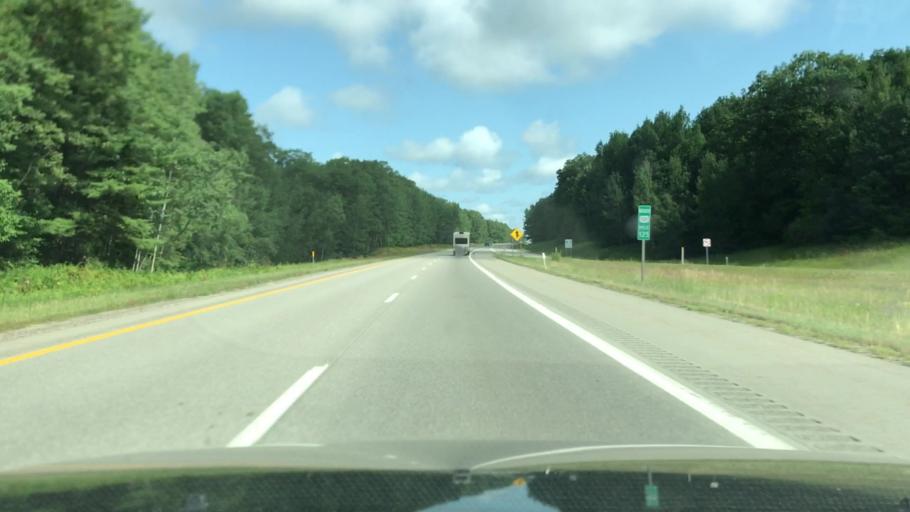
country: US
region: Michigan
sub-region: Montcalm County
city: Howard City
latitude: 43.4931
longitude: -85.4850
